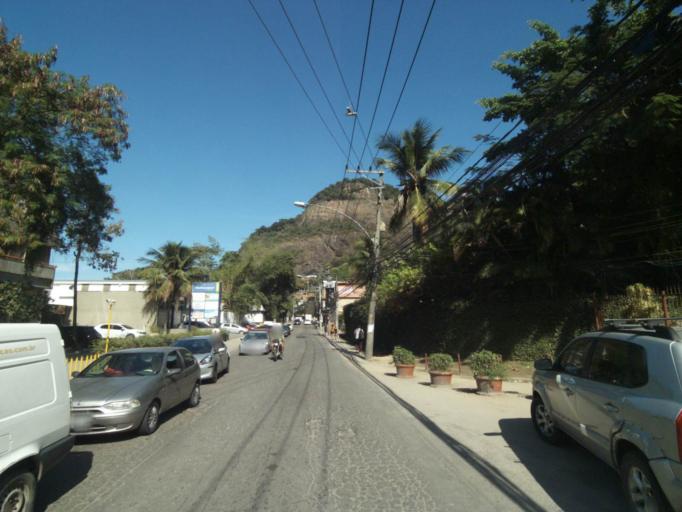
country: BR
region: Rio de Janeiro
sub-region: Rio De Janeiro
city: Rio de Janeiro
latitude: -22.9889
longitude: -43.3112
